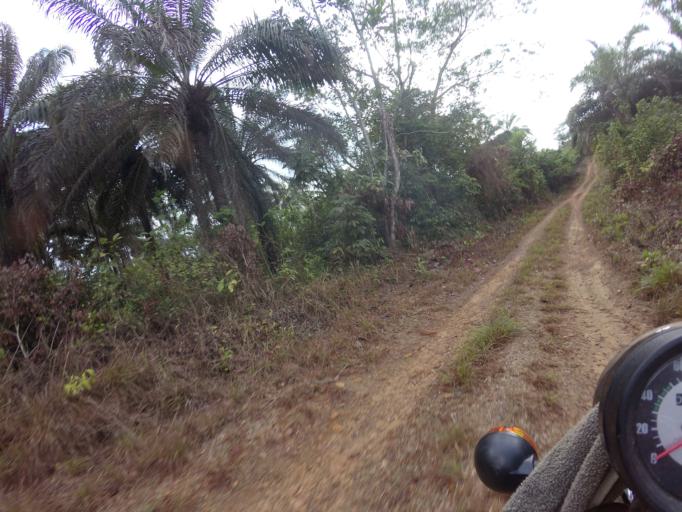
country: SL
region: Southern Province
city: Zimmi
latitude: 7.1516
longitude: -11.2089
